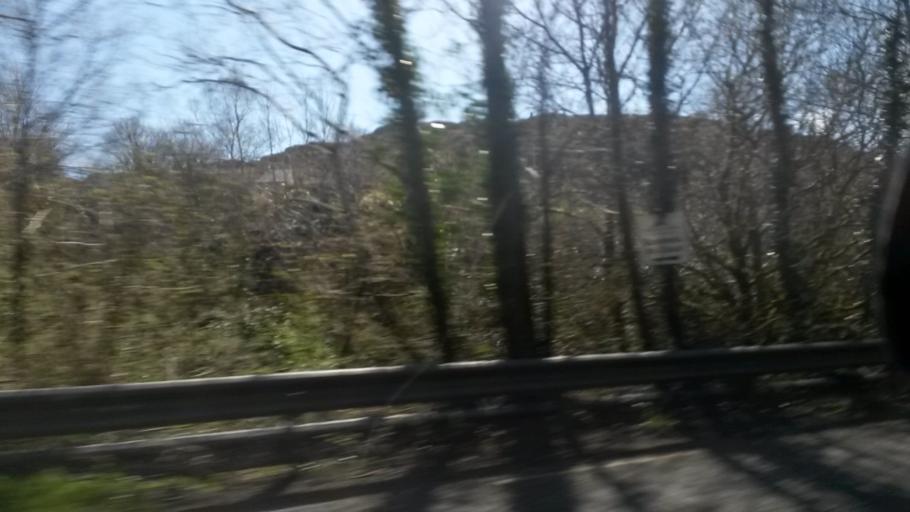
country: IE
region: Munster
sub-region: Ciarrai
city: Cill Airne
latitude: 51.9249
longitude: -9.3844
